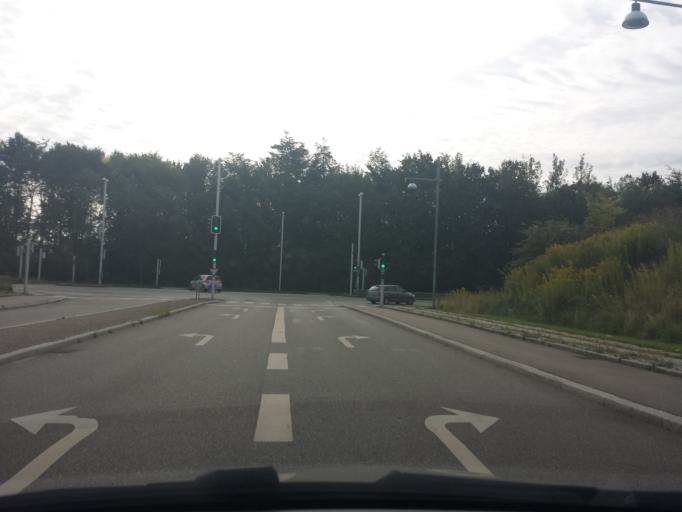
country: DK
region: Capital Region
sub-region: Glostrup Kommune
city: Glostrup
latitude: 55.6976
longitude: 12.4130
